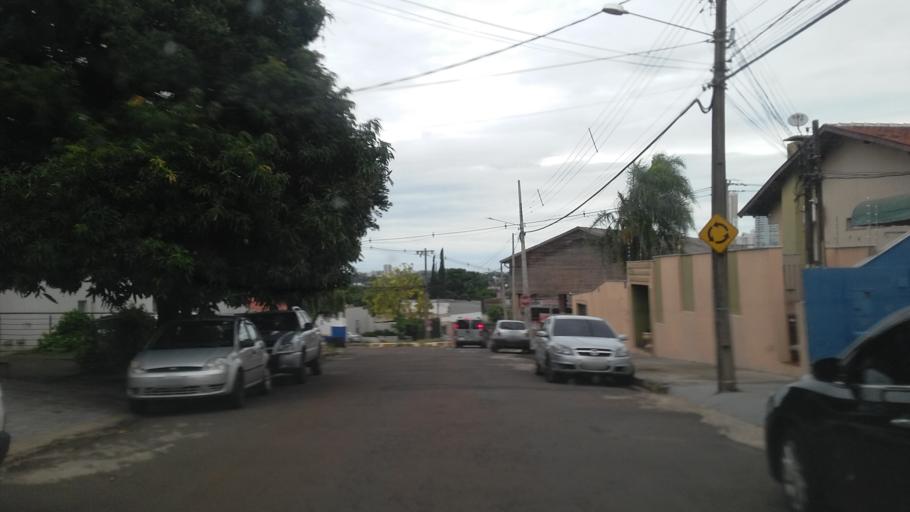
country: BR
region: Parana
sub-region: Londrina
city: Londrina
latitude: -23.3198
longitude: -51.1772
